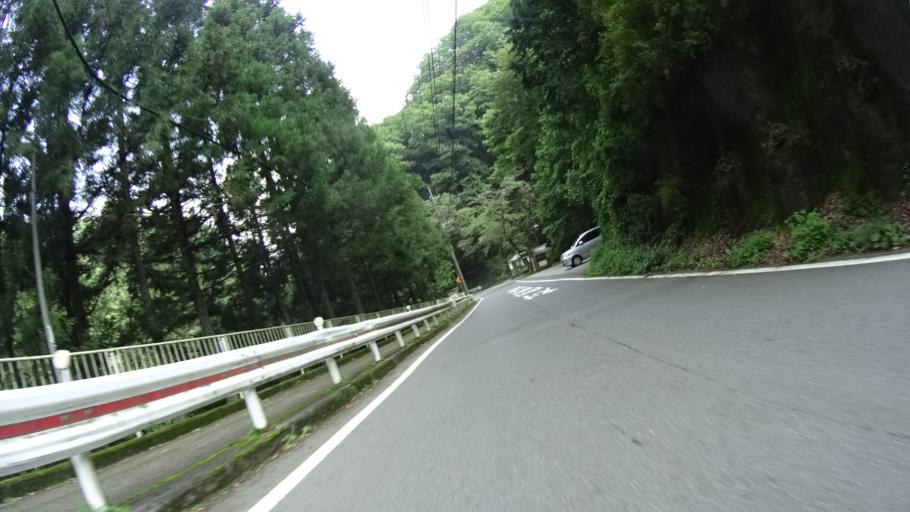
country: JP
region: Gunma
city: Tomioka
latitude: 36.0715
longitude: 138.8298
